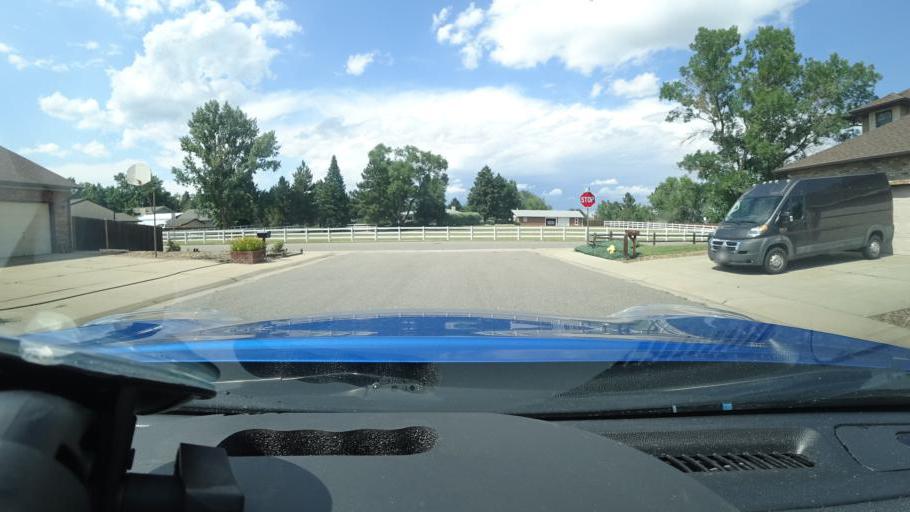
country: US
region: Colorado
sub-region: Adams County
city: Aurora
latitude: 39.6782
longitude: -104.8572
